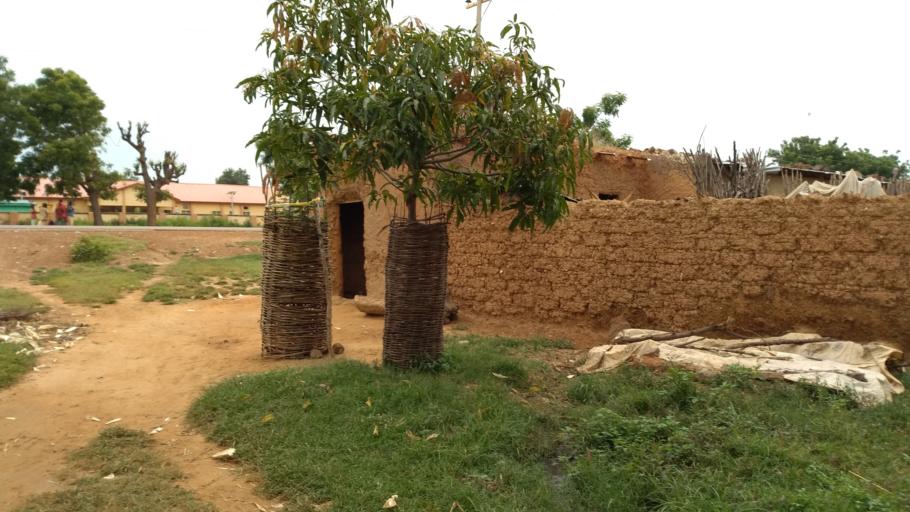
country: NG
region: Kano
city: Tsanyawa
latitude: 12.3124
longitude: 7.8610
